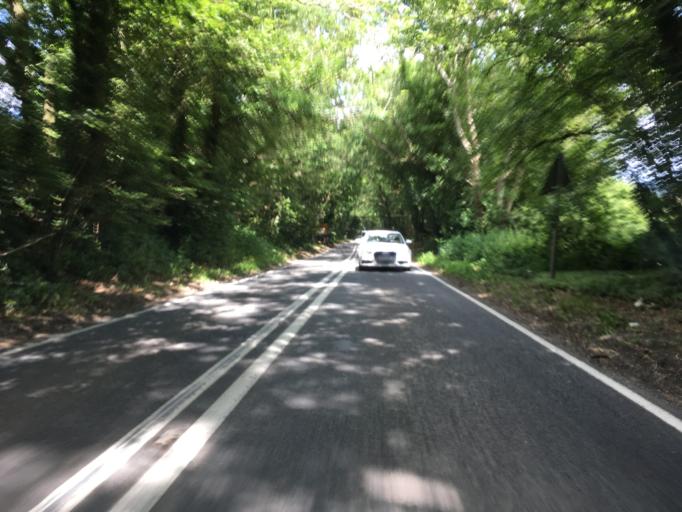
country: GB
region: England
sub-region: Hampshire
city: Highclere
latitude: 51.3171
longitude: -1.3830
